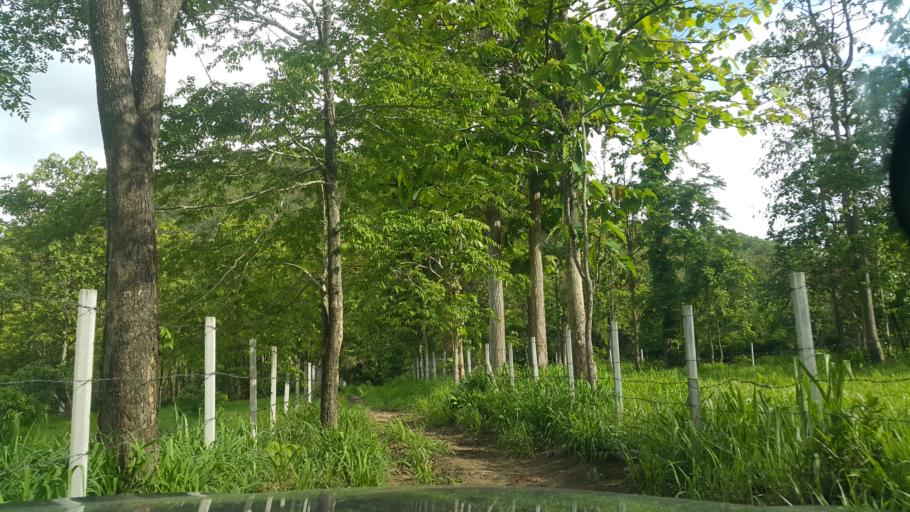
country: TH
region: Chiang Mai
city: Mae On
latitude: 18.7093
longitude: 99.2156
